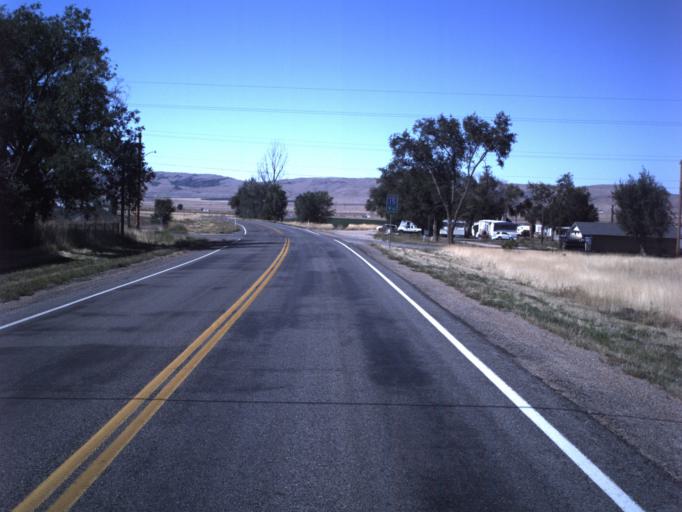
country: US
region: Utah
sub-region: Juab County
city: Nephi
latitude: 39.5589
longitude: -111.8667
